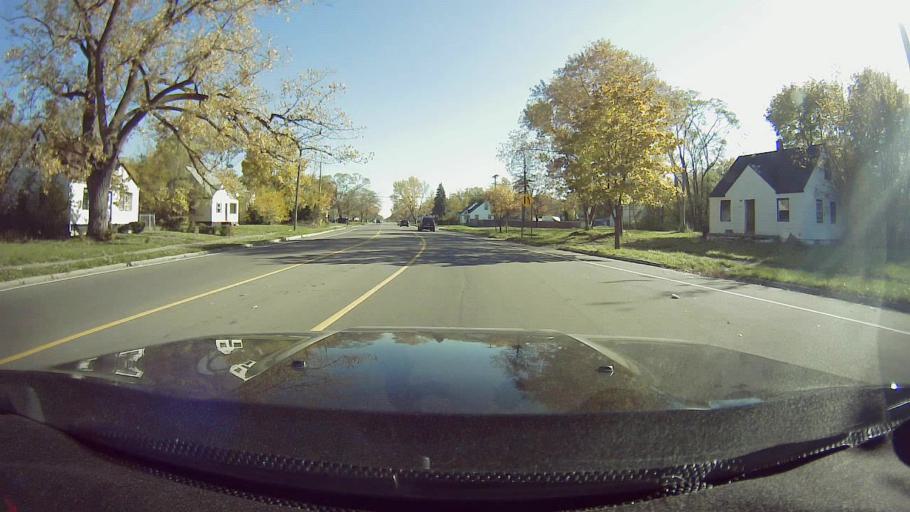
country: US
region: Michigan
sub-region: Wayne County
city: Dearborn
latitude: 42.3651
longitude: -83.2152
